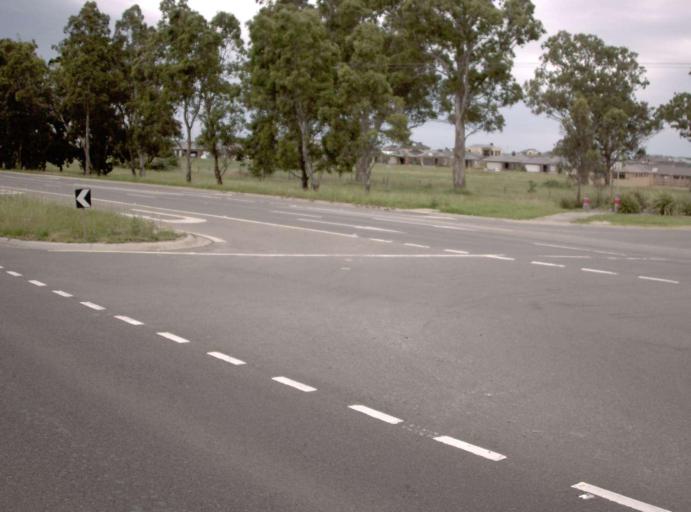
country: AU
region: Victoria
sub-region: Casey
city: Lynbrook
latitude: -38.0548
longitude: 145.2606
